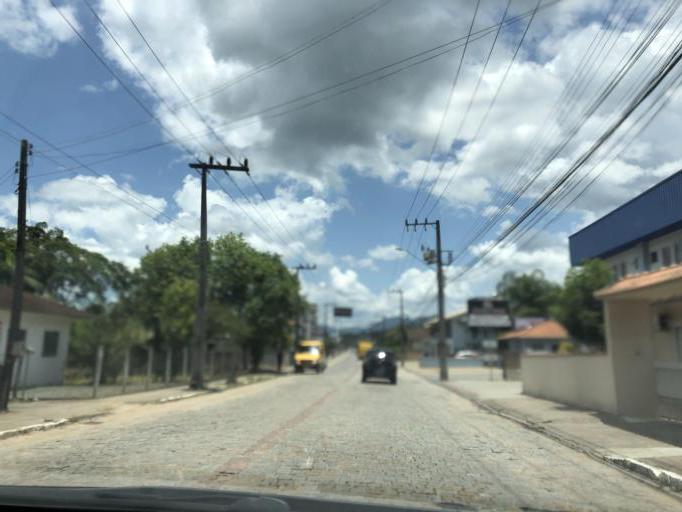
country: BR
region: Santa Catarina
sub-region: Jaragua Do Sul
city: Jaragua do Sul
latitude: -26.5159
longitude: -49.1304
